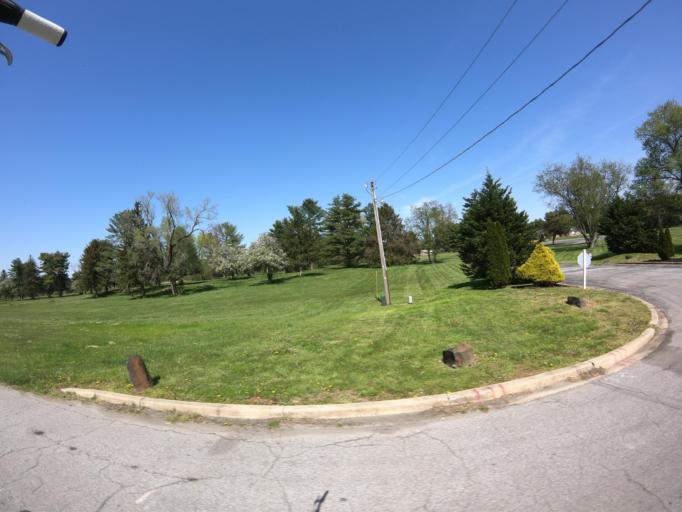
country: US
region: Maryland
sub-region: Cecil County
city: Elkton
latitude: 39.5622
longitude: -75.8075
